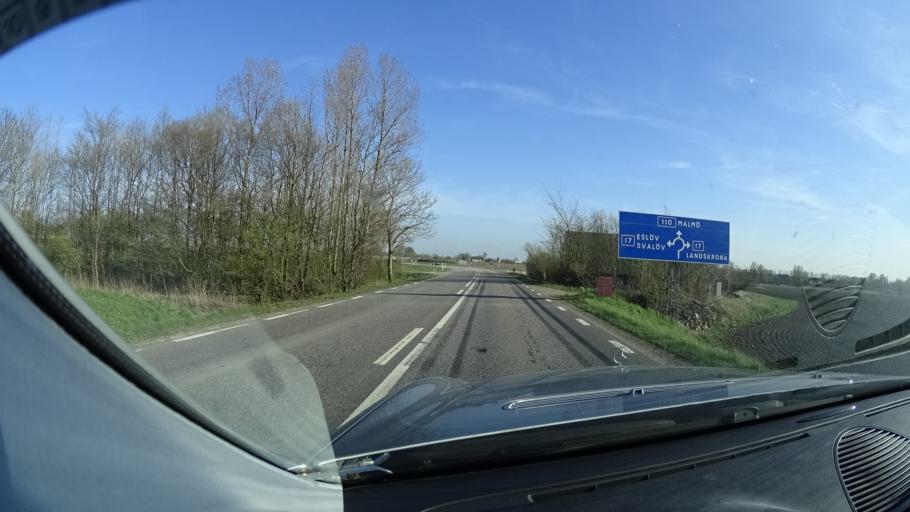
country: SE
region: Skane
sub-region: Landskrona
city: Asmundtorp
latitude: 55.8933
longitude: 12.9633
